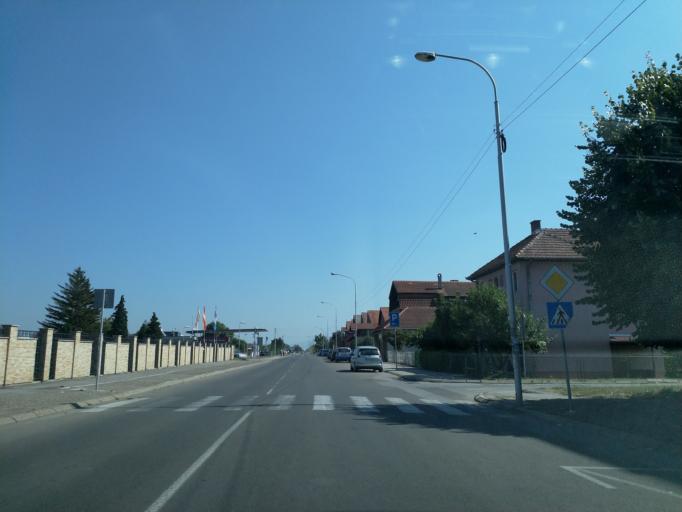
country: RS
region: Central Serbia
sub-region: Rasinski Okrug
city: Trstenik
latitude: 43.6163
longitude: 21.0106
